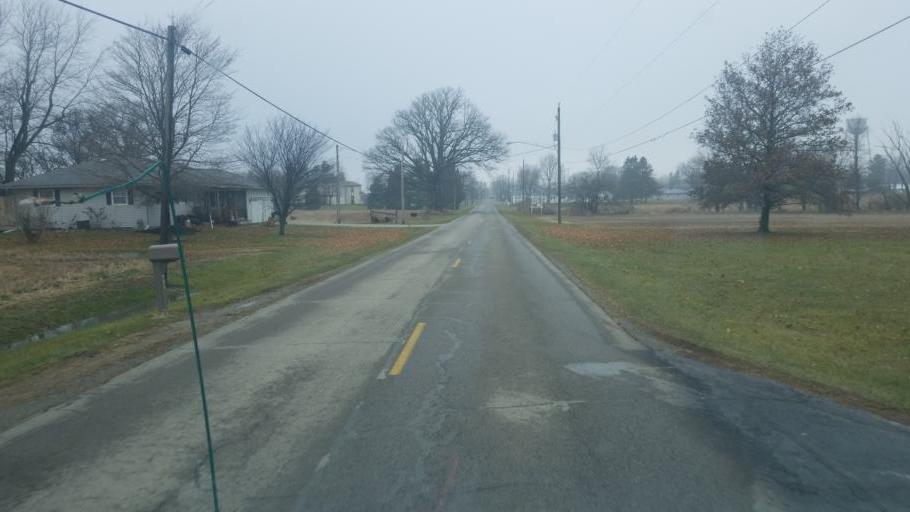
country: US
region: Ohio
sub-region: Hardin County
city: Kenton
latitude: 40.5285
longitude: -83.5246
